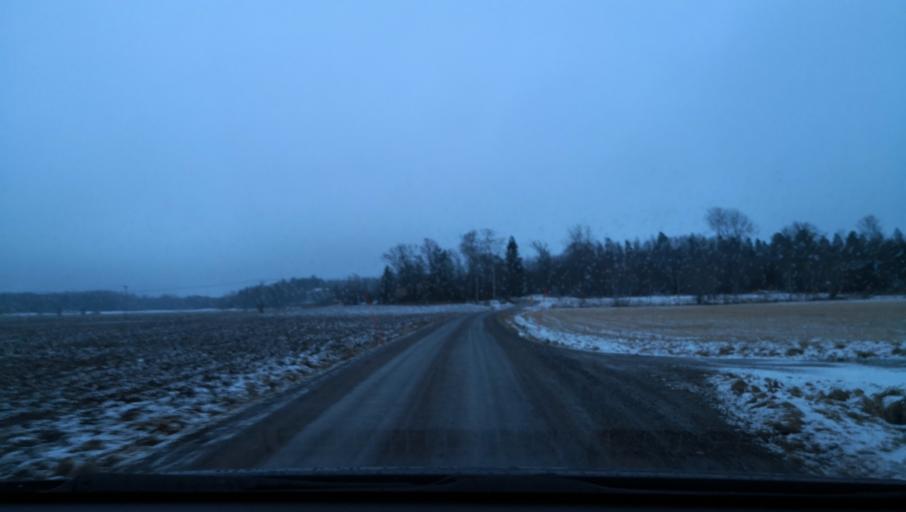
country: SE
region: Vaestmanland
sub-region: Kungsors Kommun
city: Kungsoer
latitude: 59.4087
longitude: 16.2024
